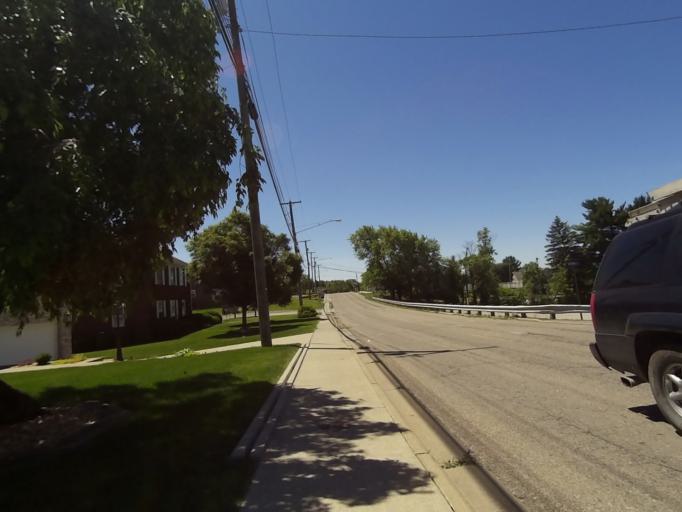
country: US
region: Ohio
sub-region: Jefferson County
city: Wintersville
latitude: 40.3731
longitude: -80.6985
